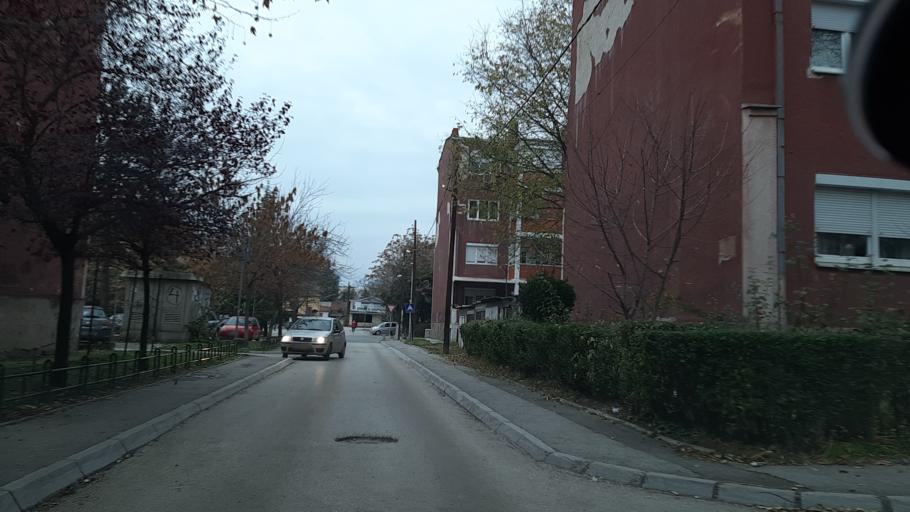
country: MK
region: Karpos
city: Skopje
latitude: 41.9906
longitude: 21.4419
